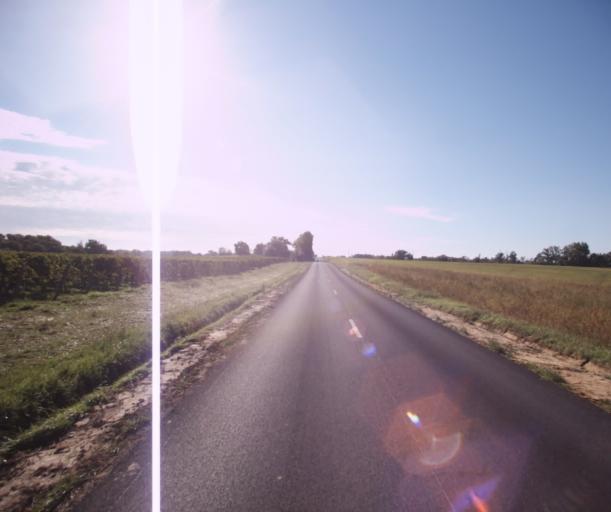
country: FR
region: Midi-Pyrenees
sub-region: Departement du Gers
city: Cazaubon
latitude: 43.9042
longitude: -0.0177
